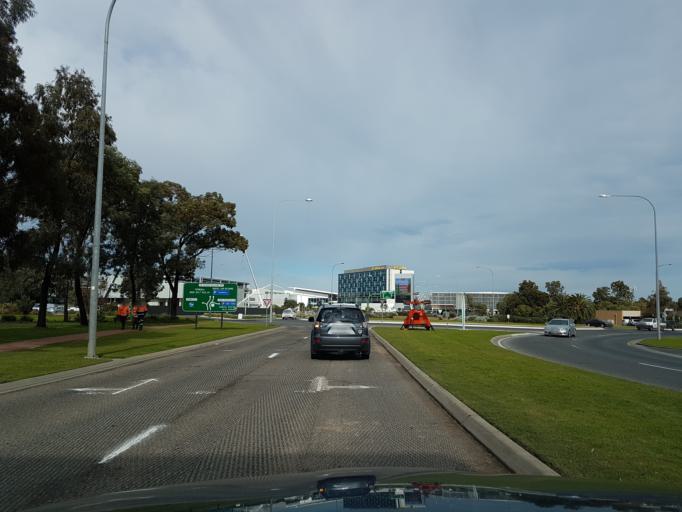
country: AU
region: South Australia
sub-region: City of West Torrens
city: Plympton
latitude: -34.9349
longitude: 138.5402
